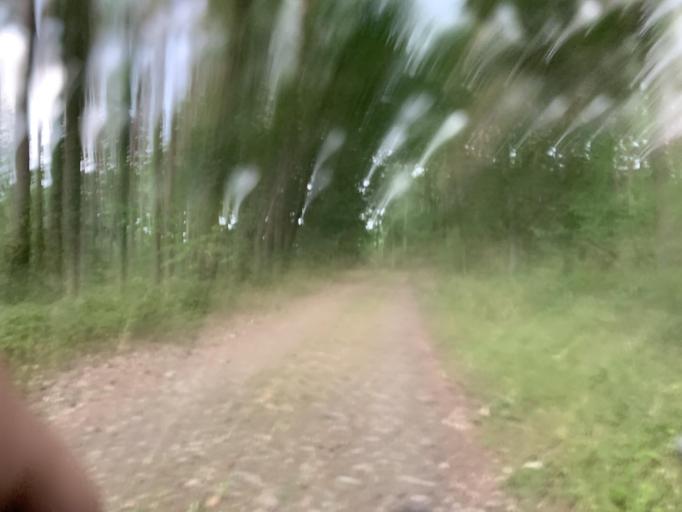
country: DE
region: Lower Saxony
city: Reinstorf
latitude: 53.2198
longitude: 10.6161
